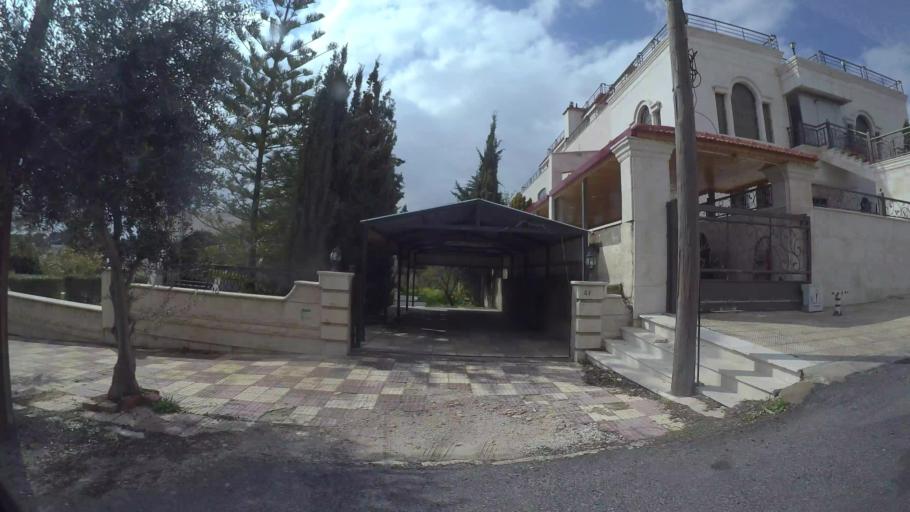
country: JO
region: Amman
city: Al Jubayhah
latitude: 32.0330
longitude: 35.8198
